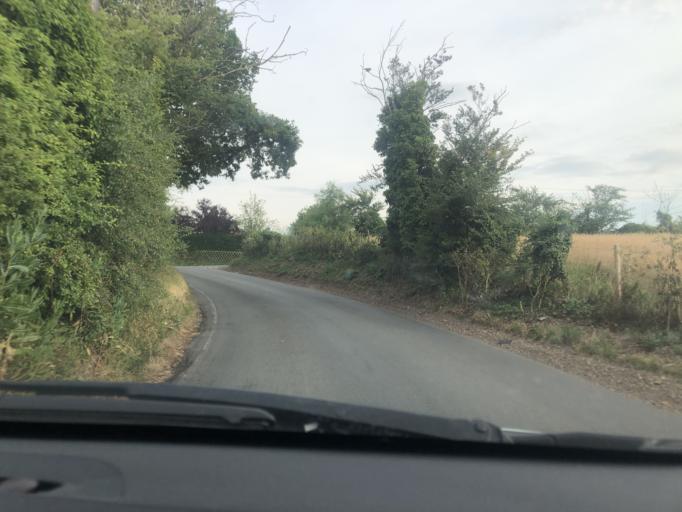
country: GB
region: England
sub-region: Kent
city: Herne Bay
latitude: 51.3508
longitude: 1.1642
